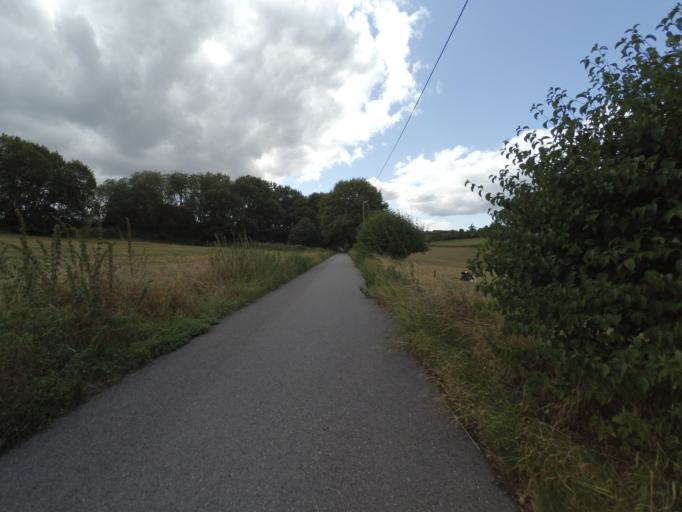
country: LU
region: Grevenmacher
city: Gonderange
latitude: 49.6748
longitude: 6.2392
